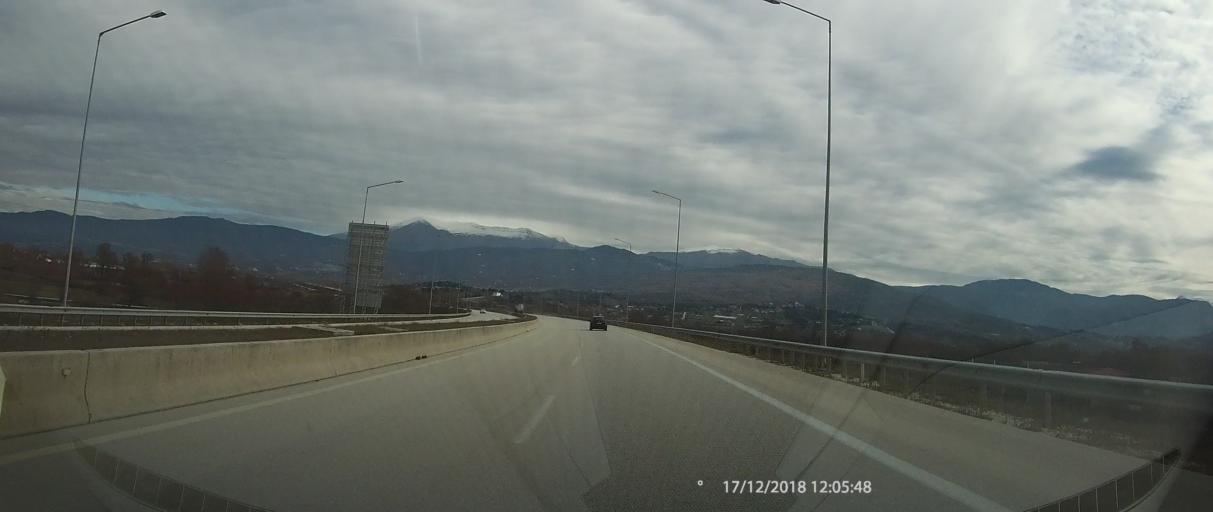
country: GR
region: Epirus
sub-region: Nomos Ioanninon
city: Koutselio
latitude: 39.5979
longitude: 20.9210
